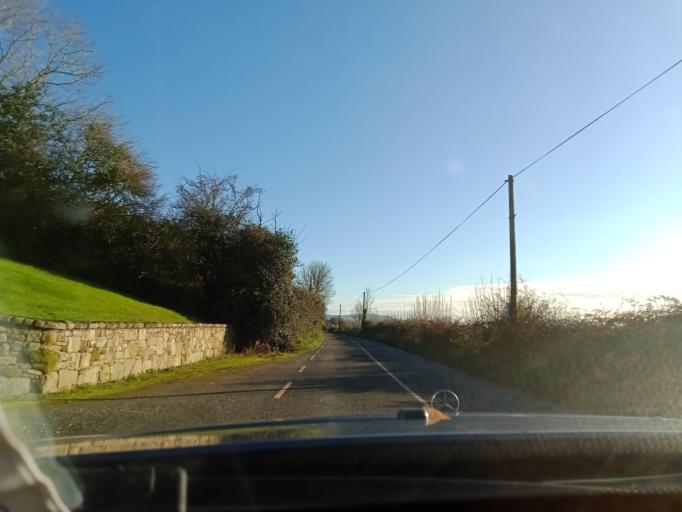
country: IE
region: Leinster
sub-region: Kilkenny
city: Piltown
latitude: 52.3959
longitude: -7.3692
